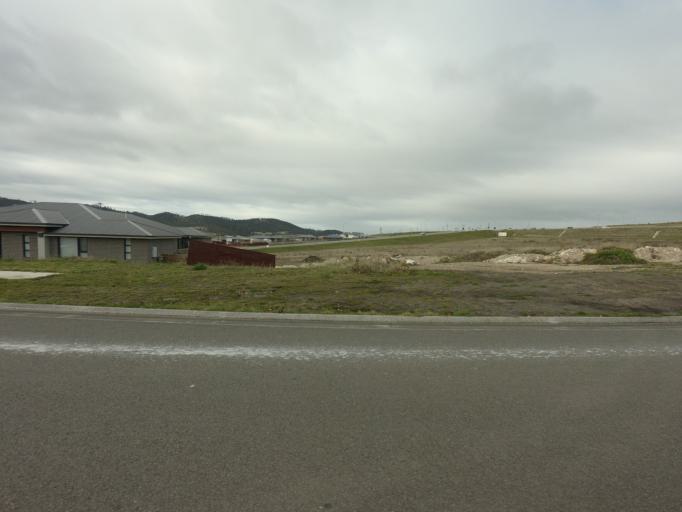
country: AU
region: Tasmania
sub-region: Clarence
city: Howrah
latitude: -42.8865
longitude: 147.4267
